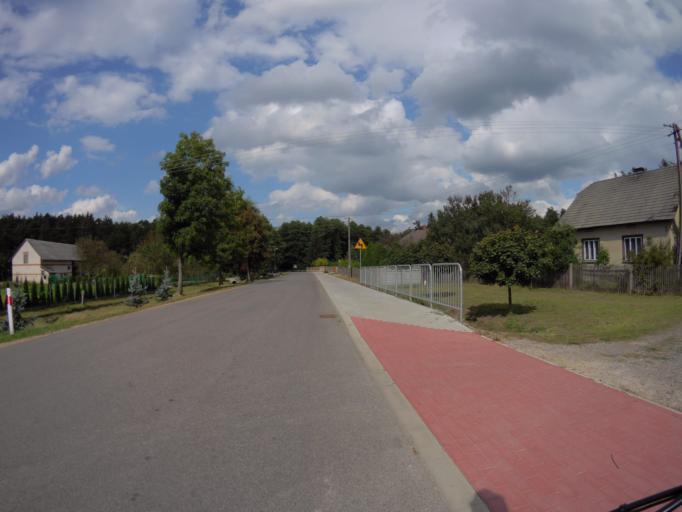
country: PL
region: Subcarpathian Voivodeship
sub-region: Powiat lezajski
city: Brzoza Krolewska
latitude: 50.2732
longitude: 22.3524
